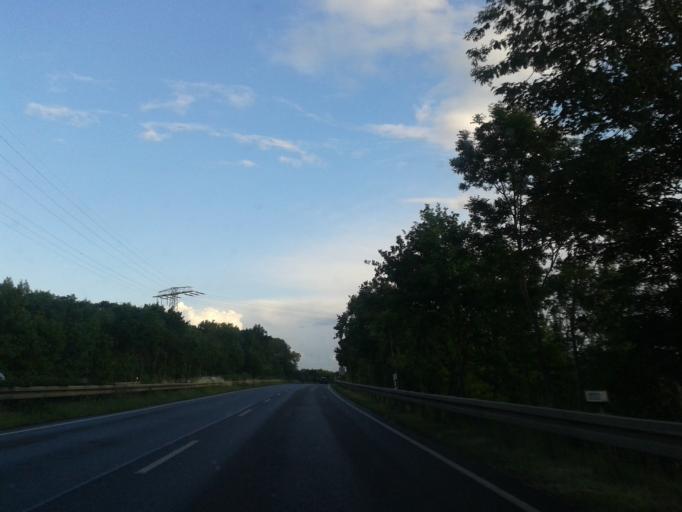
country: DE
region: Saxony
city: Markkleeberg
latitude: 51.2793
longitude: 12.3834
